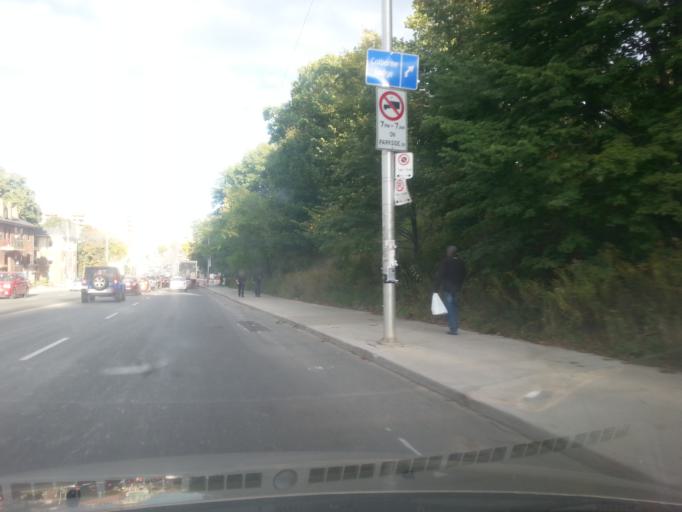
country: CA
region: Ontario
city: Toronto
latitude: 43.6542
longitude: -79.4621
